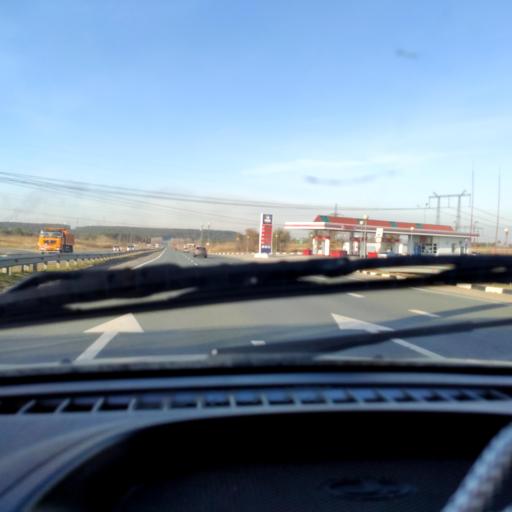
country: RU
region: Samara
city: Zhigulevsk
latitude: 53.5177
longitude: 49.5352
